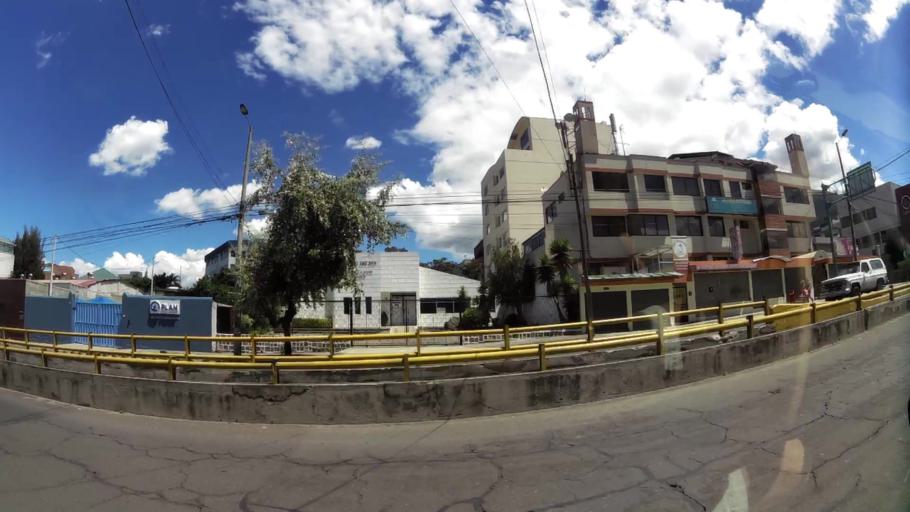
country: EC
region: Pichincha
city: Quito
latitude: -0.1809
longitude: -78.4906
